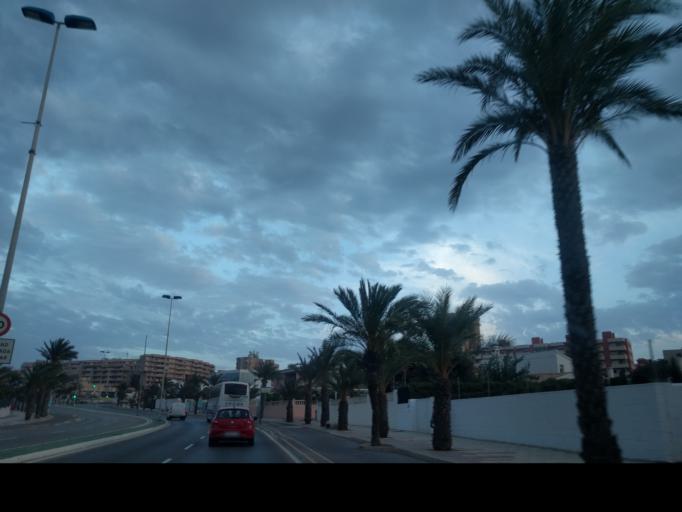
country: ES
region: Murcia
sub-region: Murcia
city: La Manga del Mar Menor
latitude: 37.6683
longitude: -0.7289
